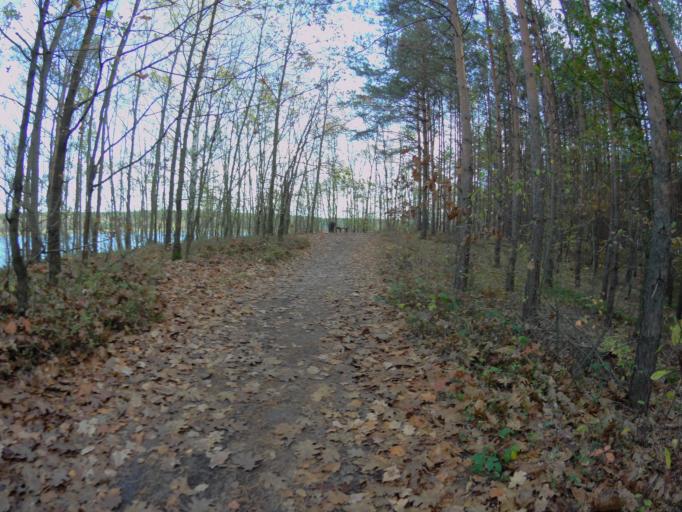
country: PL
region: Subcarpathian Voivodeship
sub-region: Powiat kolbuszowski
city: Lipnica
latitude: 50.3360
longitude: 21.9366
